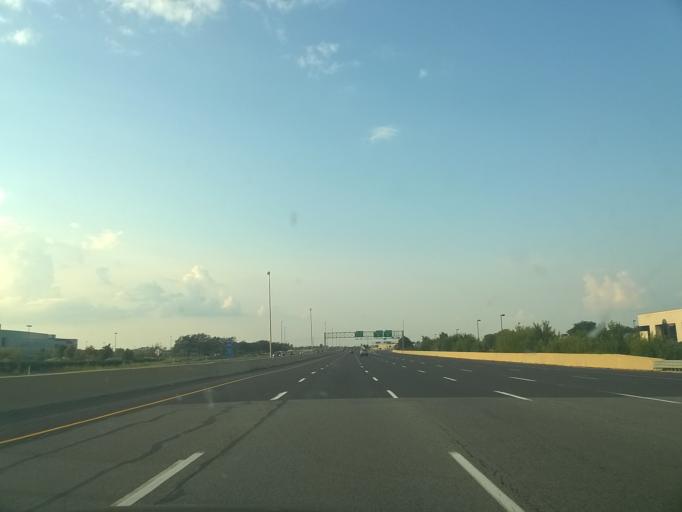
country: US
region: Indiana
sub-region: Marion County
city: Speedway
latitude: 39.8757
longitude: -86.2687
